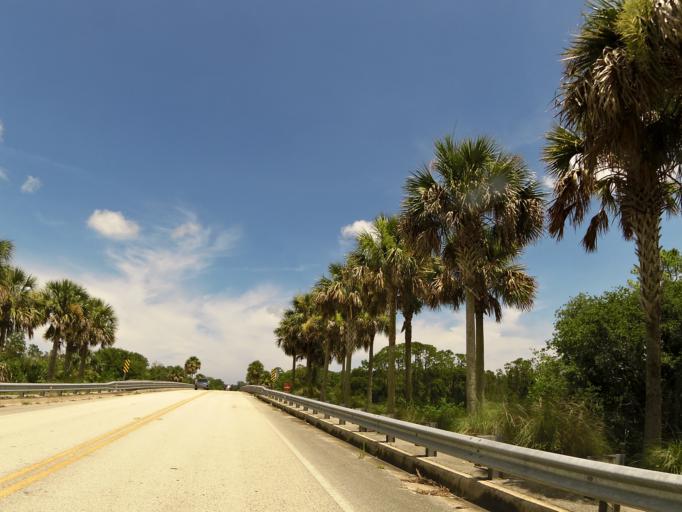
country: US
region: Florida
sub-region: Flagler County
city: Flagler Beach
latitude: 29.4037
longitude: -81.1561
